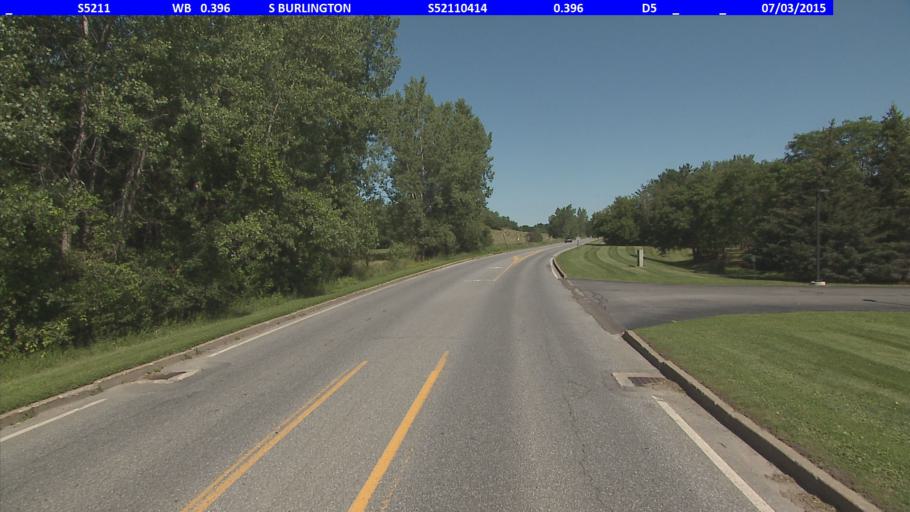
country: US
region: Vermont
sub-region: Chittenden County
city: South Burlington
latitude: 44.4557
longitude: -73.1498
